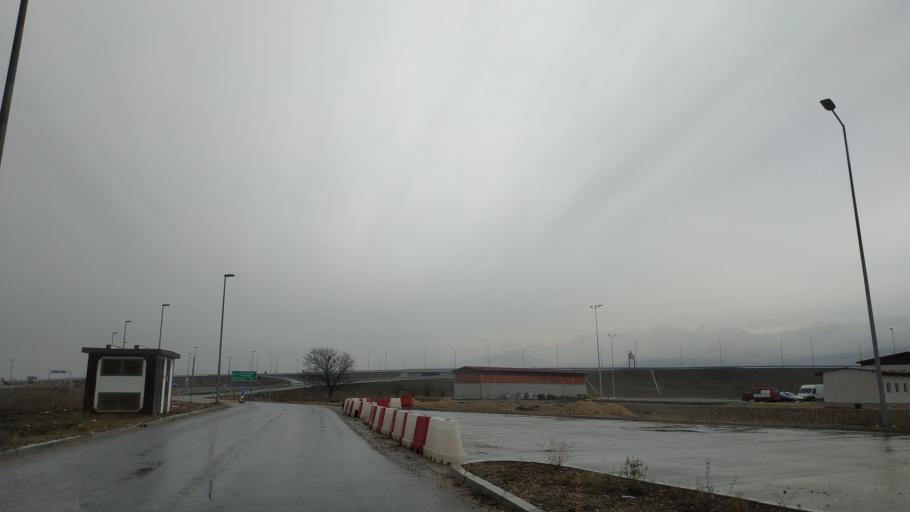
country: RS
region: Central Serbia
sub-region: Pirotski Okrug
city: Pirot
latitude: 43.1234
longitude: 22.6191
